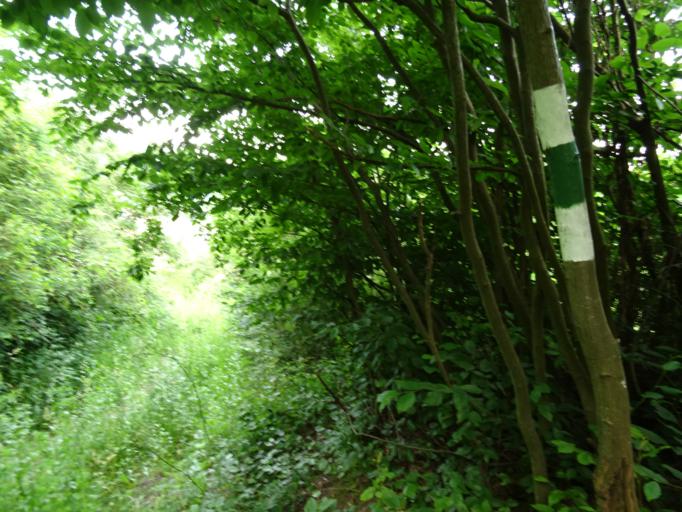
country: HU
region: Borsod-Abauj-Zemplen
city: Szendro
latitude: 48.4743
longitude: 20.6820
